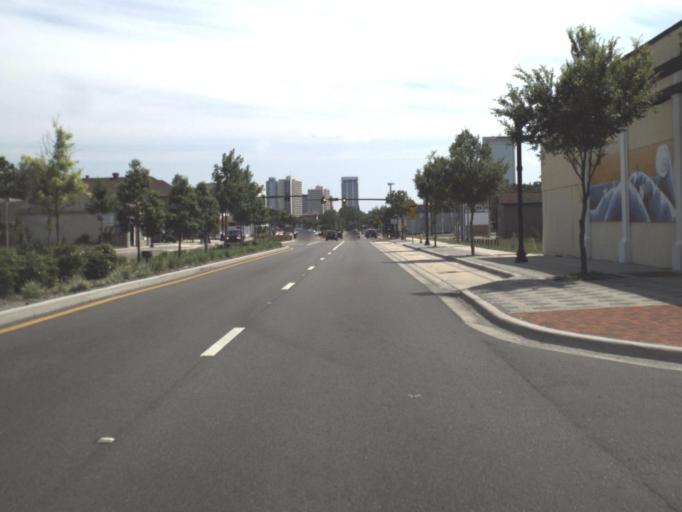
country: US
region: Florida
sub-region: Duval County
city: Jacksonville
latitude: 30.3418
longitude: -81.6545
